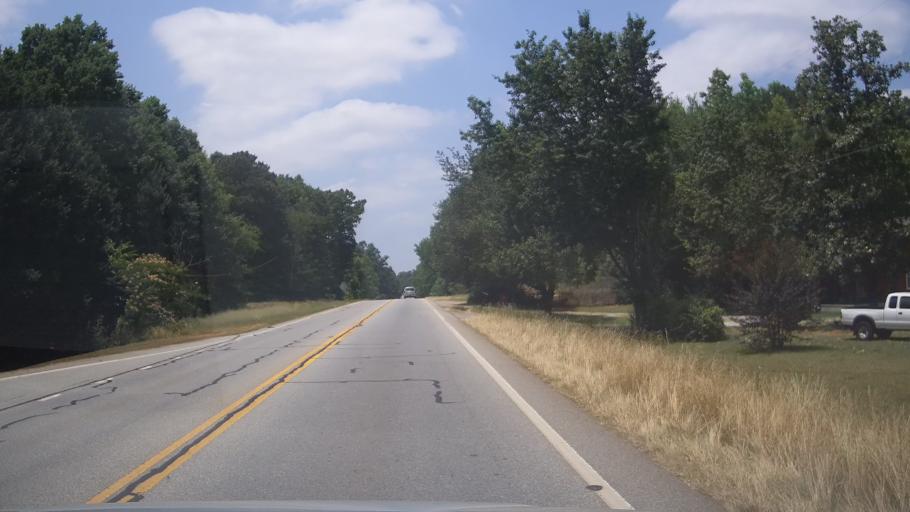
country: US
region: Georgia
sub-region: Jackson County
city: Commerce
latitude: 34.1916
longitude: -83.4107
